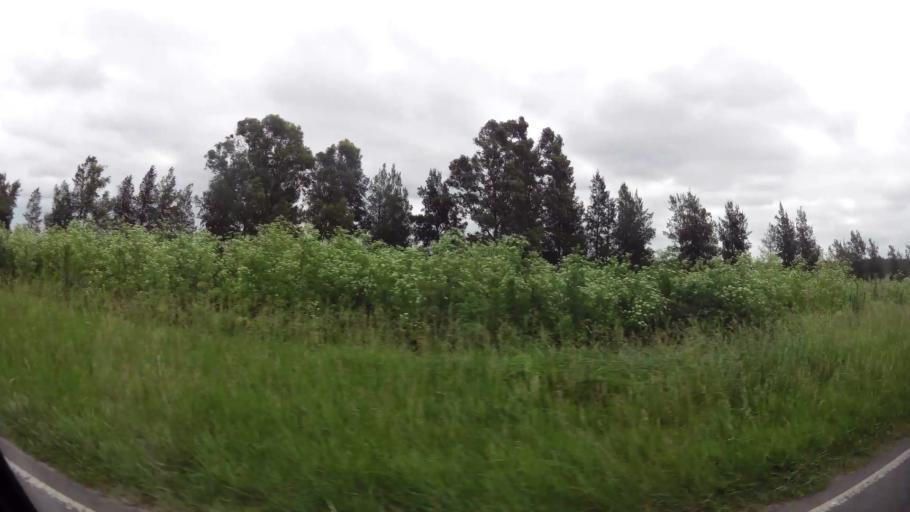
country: AR
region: Buenos Aires
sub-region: Partido de San Vicente
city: San Vicente
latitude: -35.0400
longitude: -58.4543
